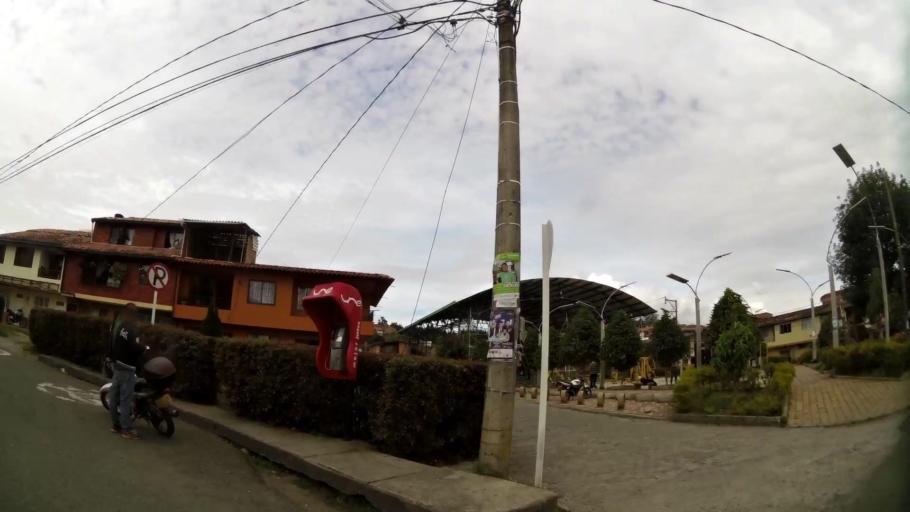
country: CO
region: Antioquia
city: Rionegro
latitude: 6.1488
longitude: -75.3879
